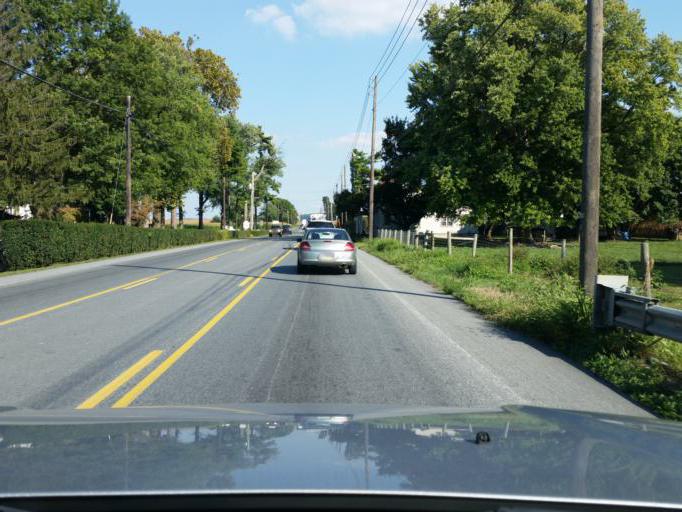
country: US
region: Pennsylvania
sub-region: Lancaster County
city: Gap
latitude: 39.9951
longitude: -76.0410
